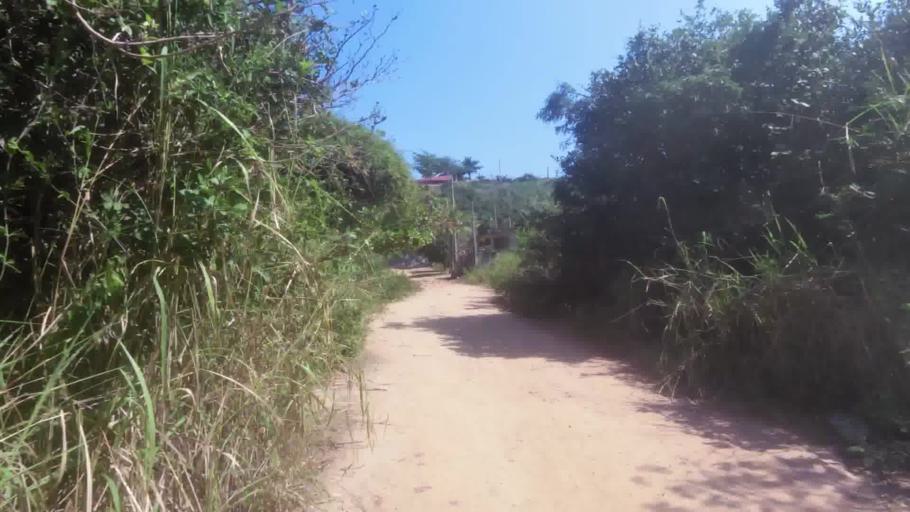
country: BR
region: Espirito Santo
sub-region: Marataizes
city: Marataizes
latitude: -21.0842
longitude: -40.8424
